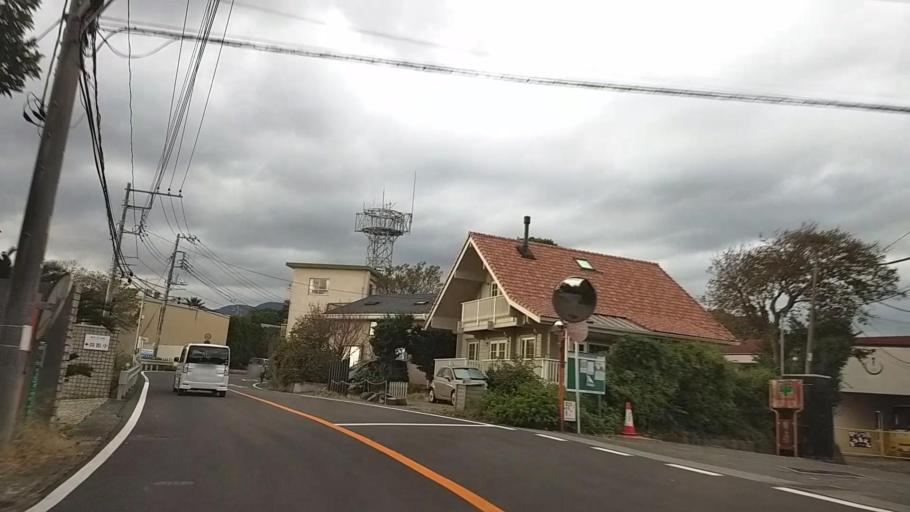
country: JP
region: Kanagawa
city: Yugawara
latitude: 35.1502
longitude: 139.1410
